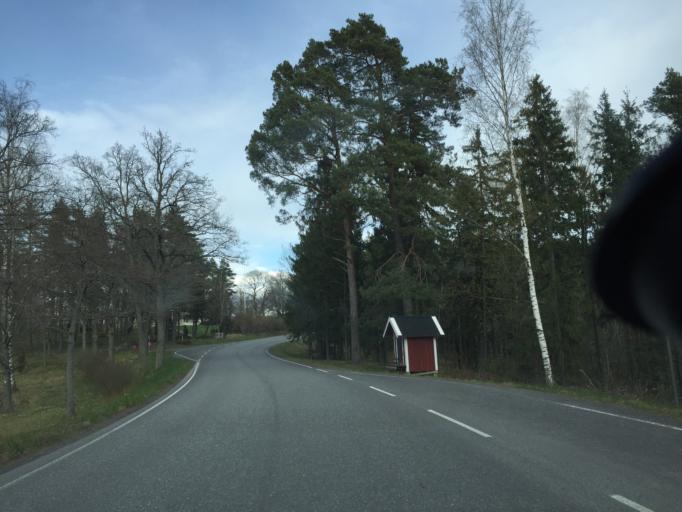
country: FI
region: Varsinais-Suomi
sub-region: Salo
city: Saerkisalo
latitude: 60.0057
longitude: 23.1044
